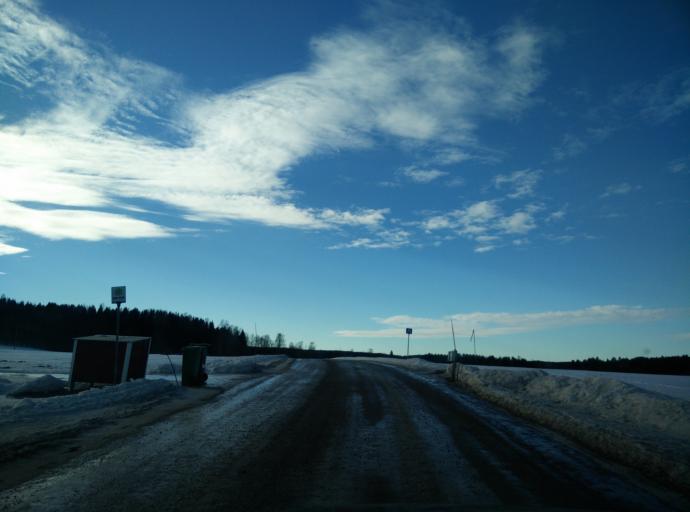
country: SE
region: Vaesternorrland
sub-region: Sundsvalls Kommun
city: Skottsund
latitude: 62.2793
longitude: 17.4013
